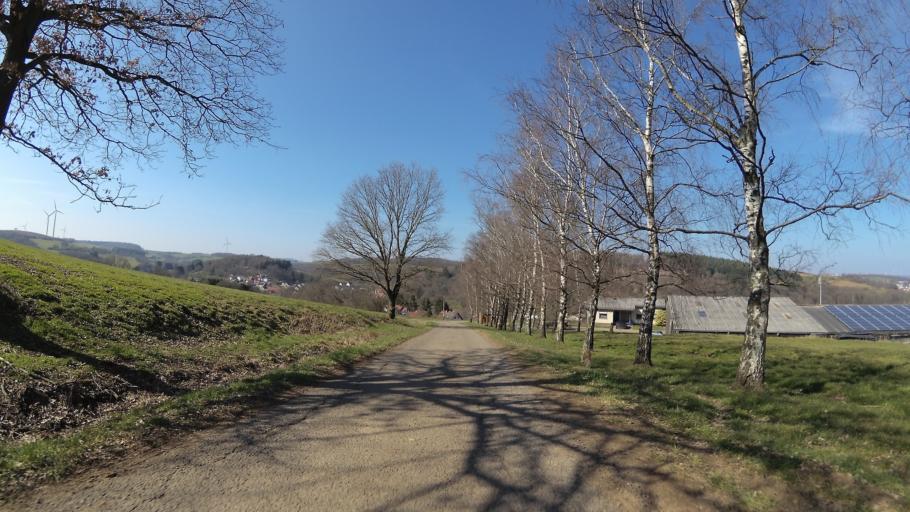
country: DE
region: Saarland
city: Marpingen
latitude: 49.4308
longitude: 7.0394
